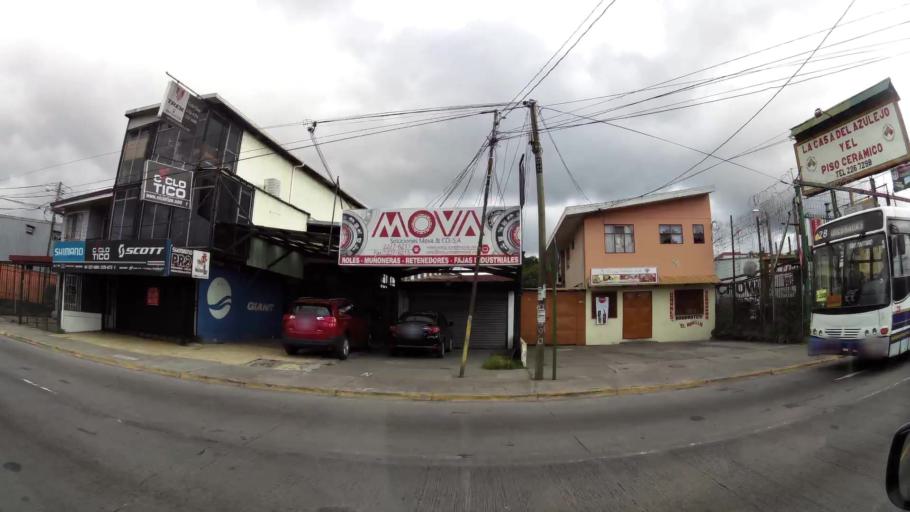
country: CR
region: San Jose
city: San Pedro
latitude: 9.9095
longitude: -84.0546
